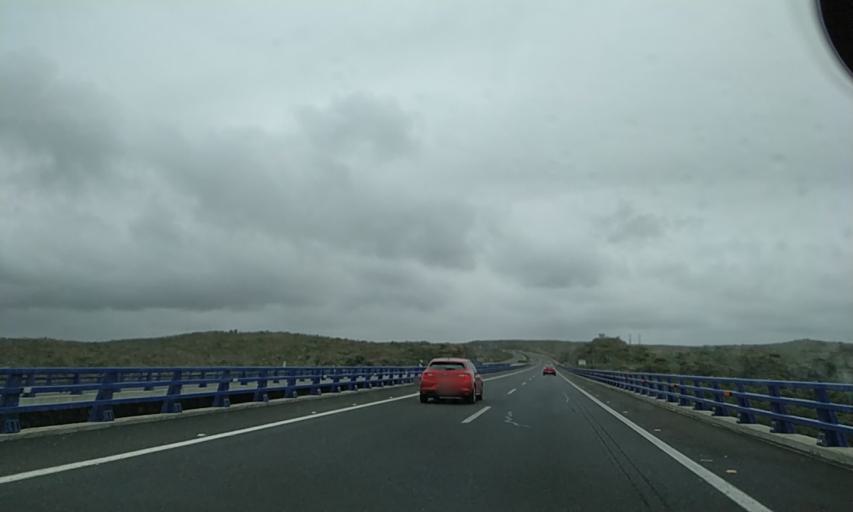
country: ES
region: Extremadura
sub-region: Provincia de Caceres
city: Hinojal
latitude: 39.7206
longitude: -6.4110
